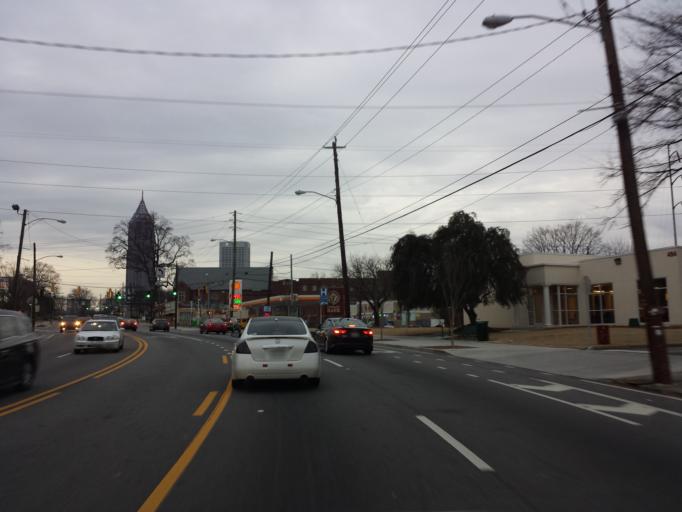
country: US
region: Georgia
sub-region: Fulton County
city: Atlanta
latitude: 33.7739
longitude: -84.3699
